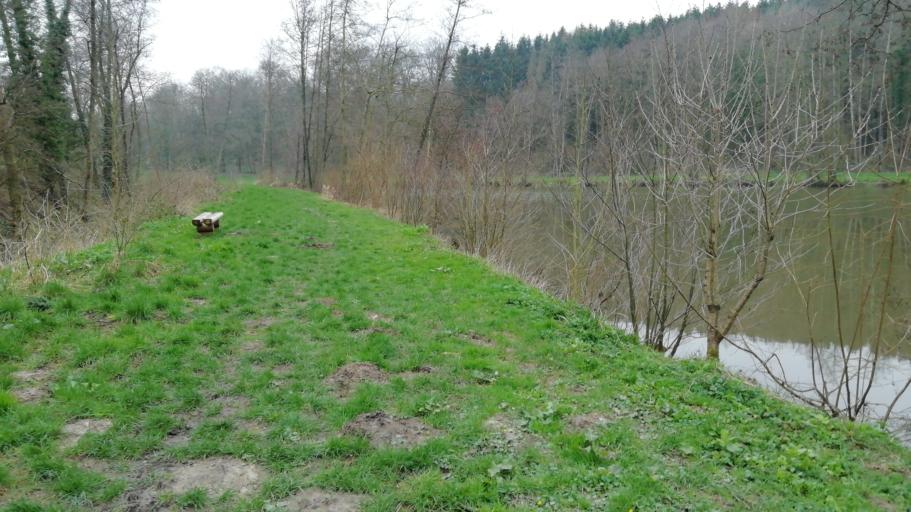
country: FR
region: Nord-Pas-de-Calais
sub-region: Departement du Nord
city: Jeumont
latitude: 50.2410
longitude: 4.1452
